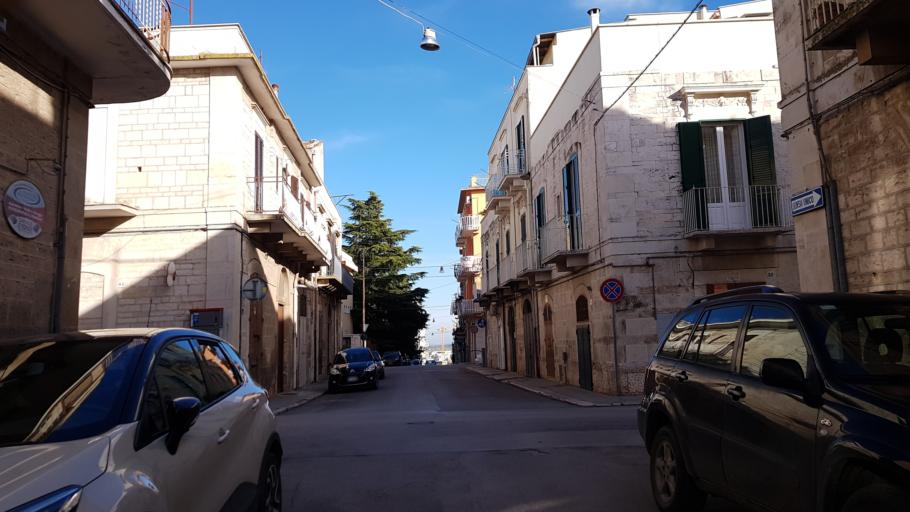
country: IT
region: Apulia
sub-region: Provincia di Bari
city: Ruvo di Puglia
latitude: 41.1201
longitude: 16.4864
